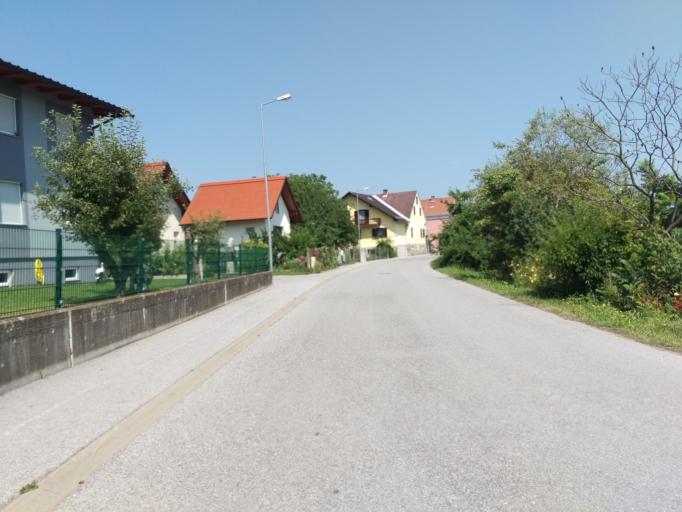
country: AT
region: Styria
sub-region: Politischer Bezirk Graz-Umgebung
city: Kalsdorf bei Graz
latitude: 46.9550
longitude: 15.4867
